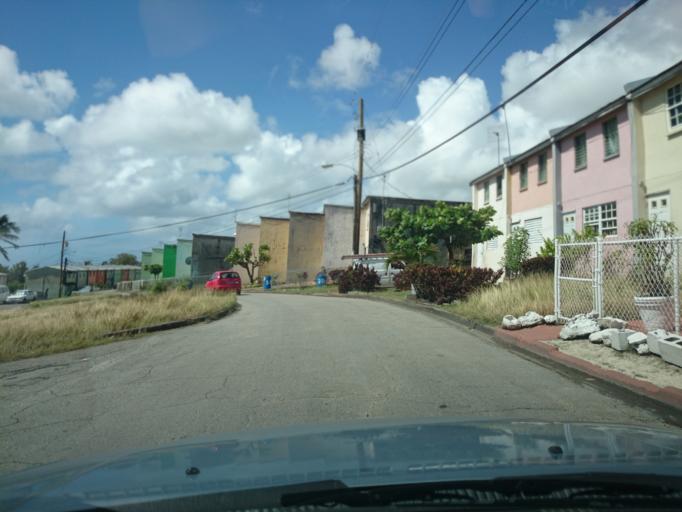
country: BB
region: Christ Church
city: Oistins
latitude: 13.0738
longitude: -59.5525
